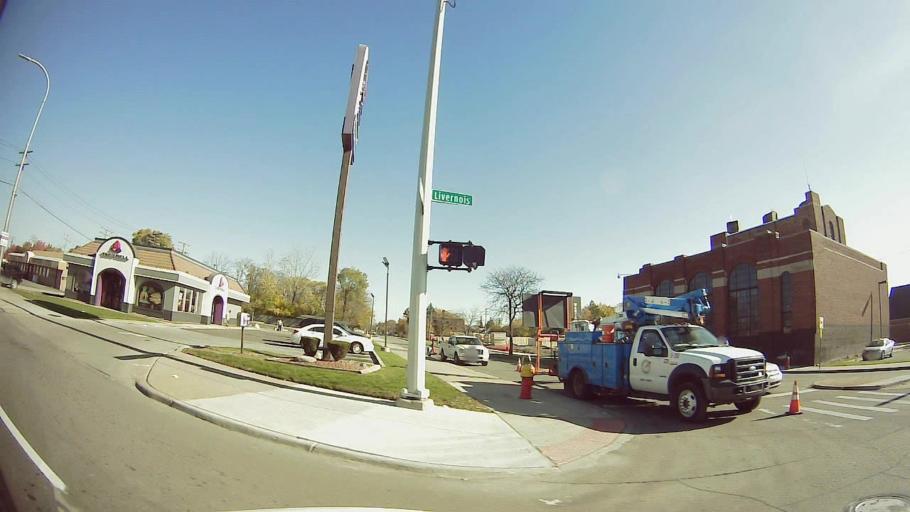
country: US
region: Michigan
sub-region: Wayne County
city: Highland Park
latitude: 42.3916
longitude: -83.1396
